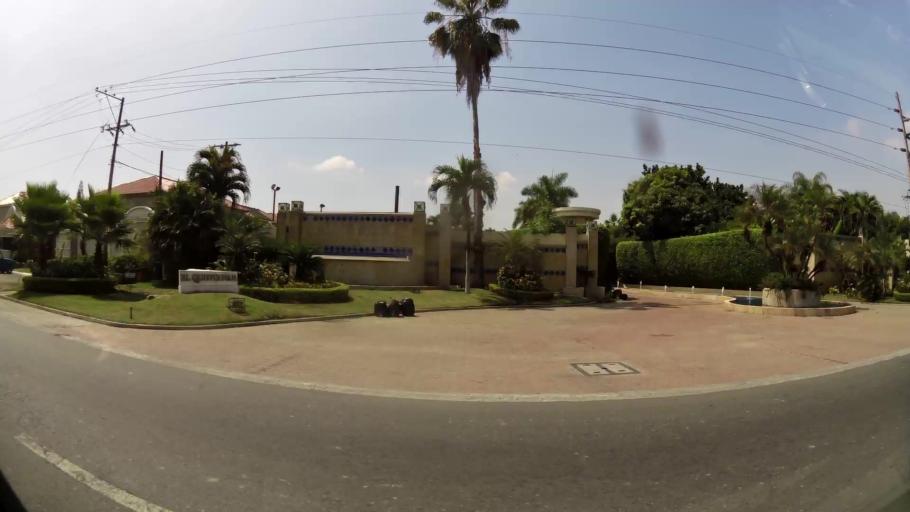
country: EC
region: Guayas
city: Eloy Alfaro
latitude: -2.1158
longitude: -79.8688
